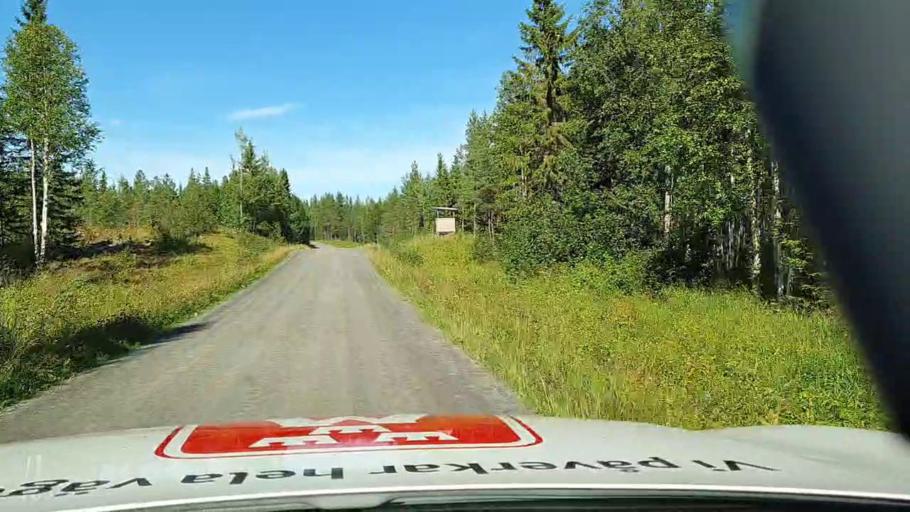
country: SE
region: Jaemtland
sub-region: OEstersunds Kommun
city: Lit
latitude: 63.7623
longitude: 14.6618
